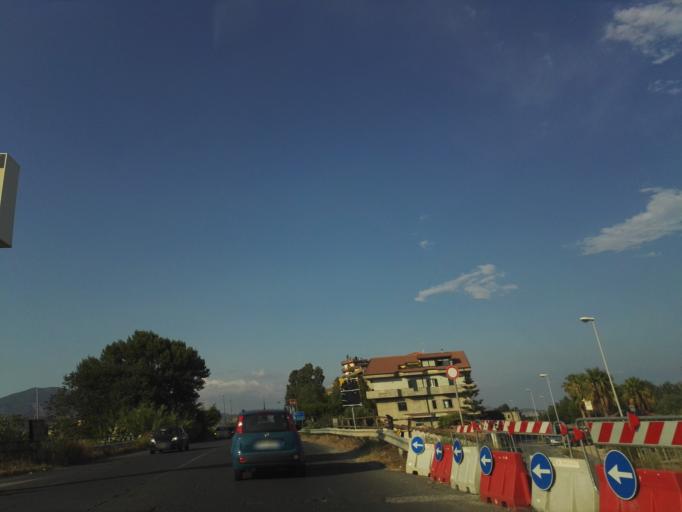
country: IT
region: Calabria
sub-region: Provincia di Reggio Calabria
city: Marina di Gioiosa Ionica
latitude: 38.2910
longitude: 16.3186
